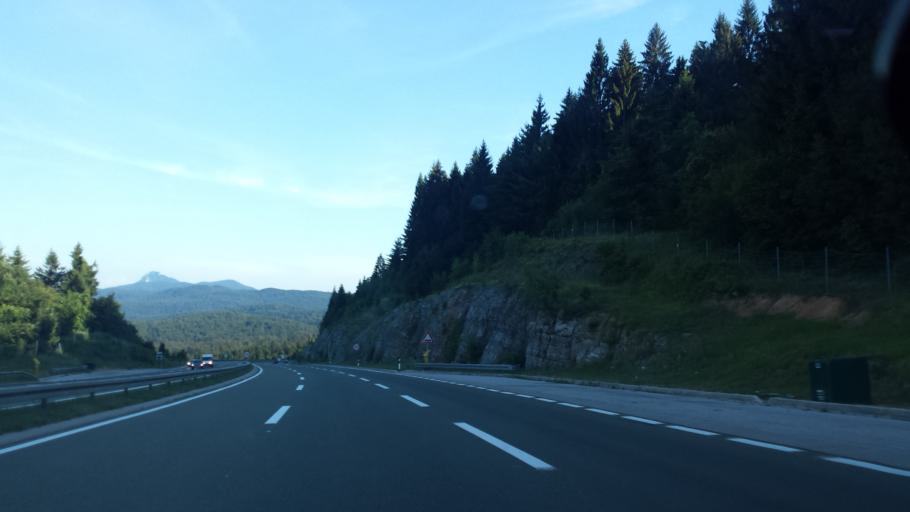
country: HR
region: Primorsko-Goranska
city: Vrbovsko
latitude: 45.3706
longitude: 15.0579
